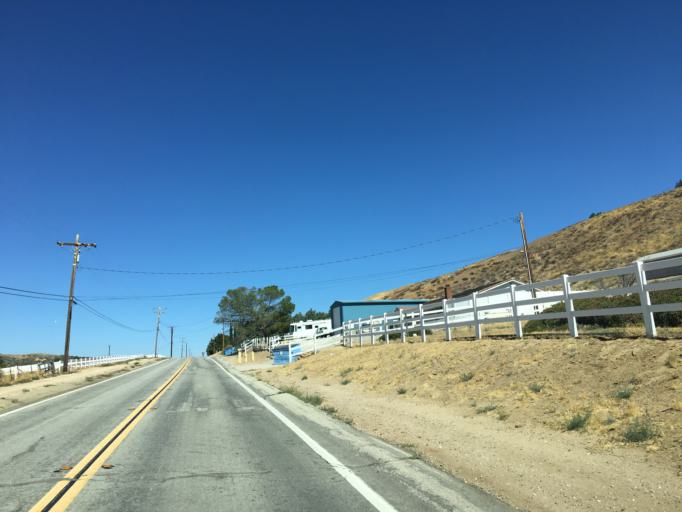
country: US
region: California
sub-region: Los Angeles County
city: Leona Valley
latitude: 34.6195
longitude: -118.2925
